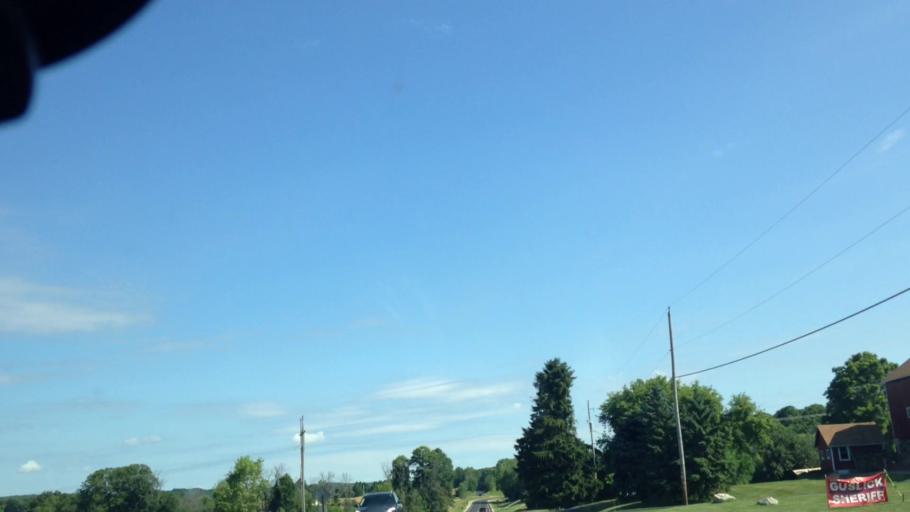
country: US
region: Wisconsin
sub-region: Washington County
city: Slinger
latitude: 43.3577
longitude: -88.2609
